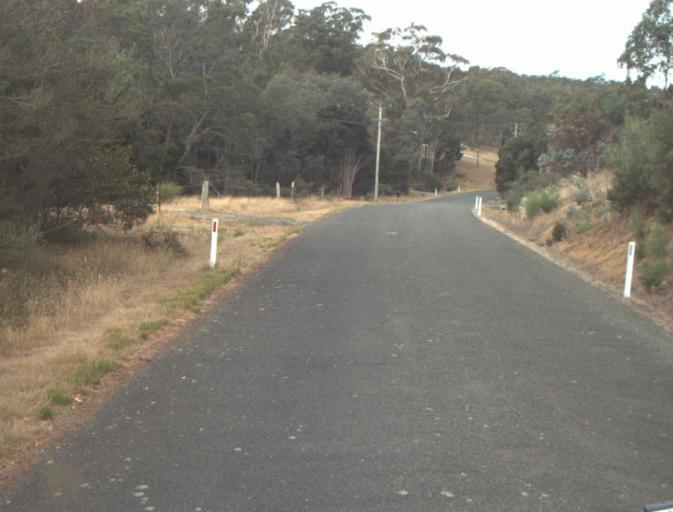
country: AU
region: Tasmania
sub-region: Launceston
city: Mayfield
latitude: -41.2792
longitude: 147.0194
